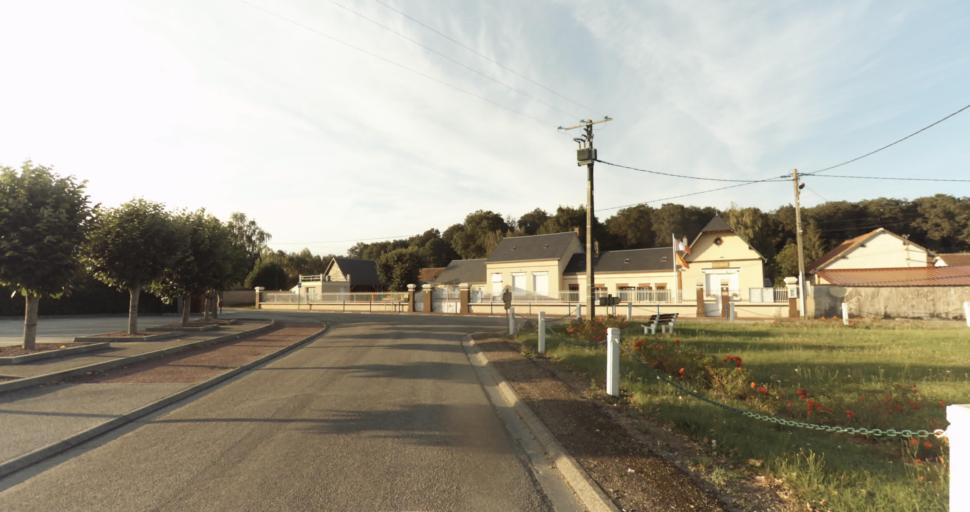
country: FR
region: Haute-Normandie
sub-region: Departement de l'Eure
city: Marcilly-sur-Eure
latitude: 48.8453
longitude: 1.2778
